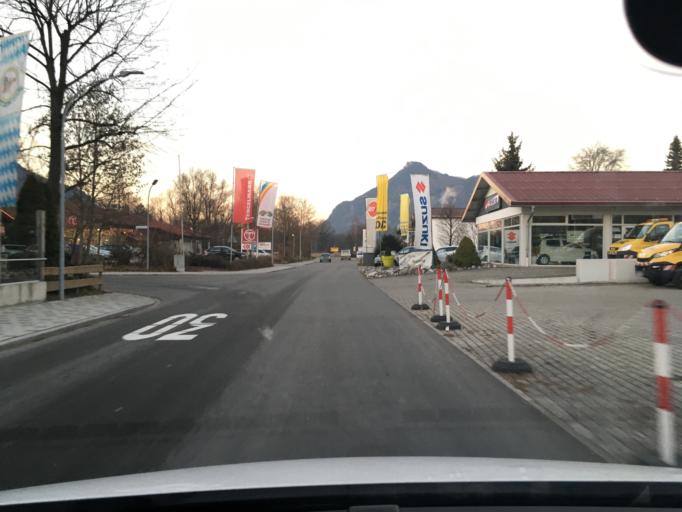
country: DE
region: Bavaria
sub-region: Upper Bavaria
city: Oberaudorf
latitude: 47.6479
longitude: 12.1790
